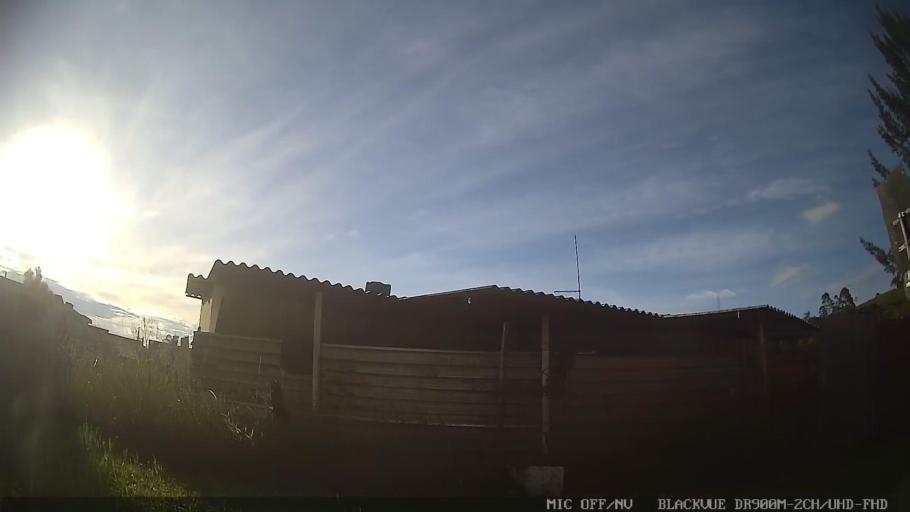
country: BR
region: Sao Paulo
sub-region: Mogi das Cruzes
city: Mogi das Cruzes
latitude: -23.5119
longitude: -46.1308
